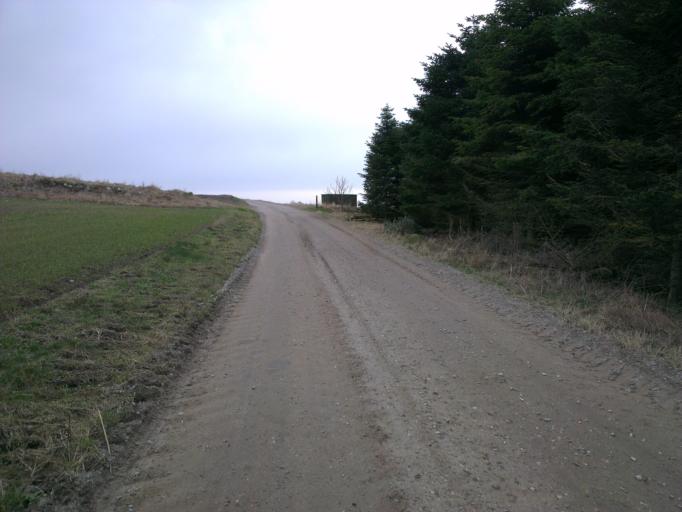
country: DK
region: Zealand
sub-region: Lejre Kommune
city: Ejby
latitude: 55.7660
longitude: 11.8745
